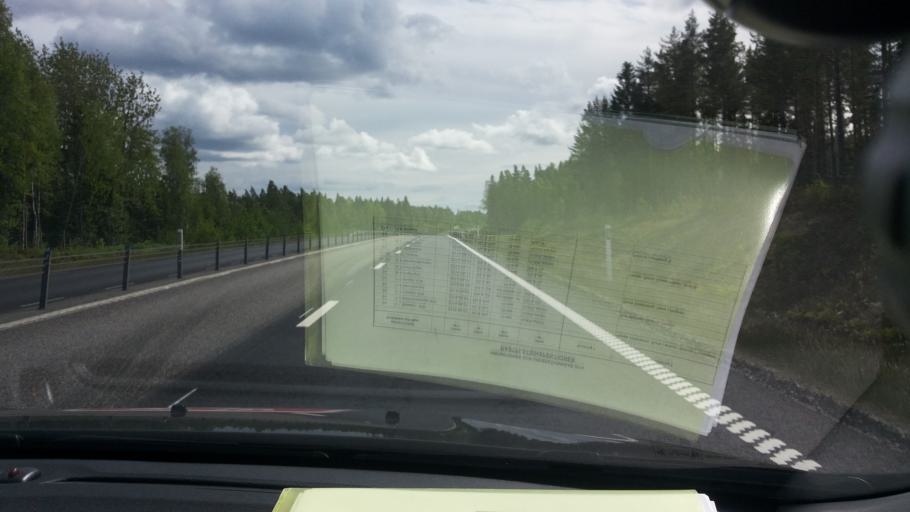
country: SE
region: Vaesternorrland
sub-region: Sundsvalls Kommun
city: Njurundabommen
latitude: 62.2160
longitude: 17.3730
